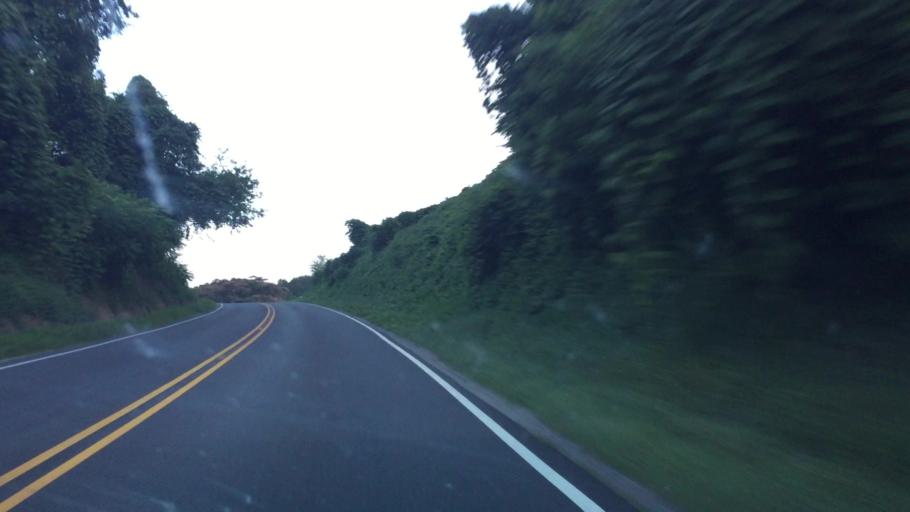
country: US
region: Virginia
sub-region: Wythe County
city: Wytheville
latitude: 36.9352
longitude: -80.9446
